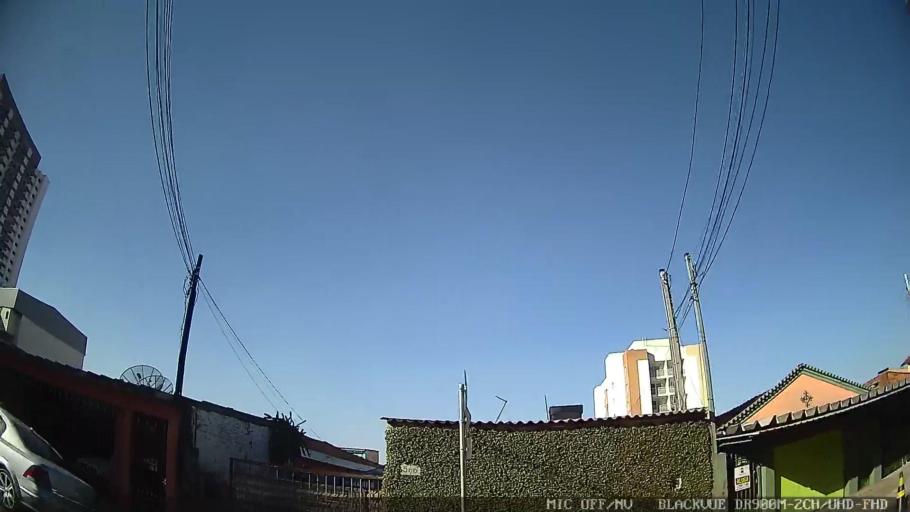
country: BR
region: Sao Paulo
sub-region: Guarulhos
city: Guarulhos
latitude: -23.5336
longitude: -46.5229
